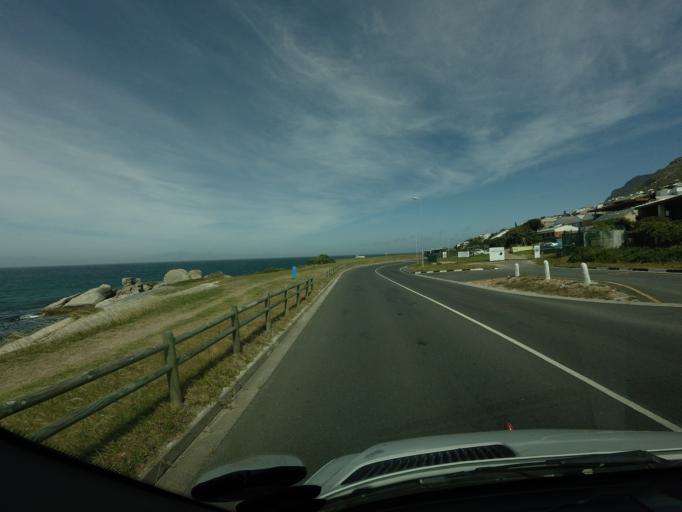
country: ZA
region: Western Cape
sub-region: City of Cape Town
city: Retreat
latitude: -34.2041
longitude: 18.4567
